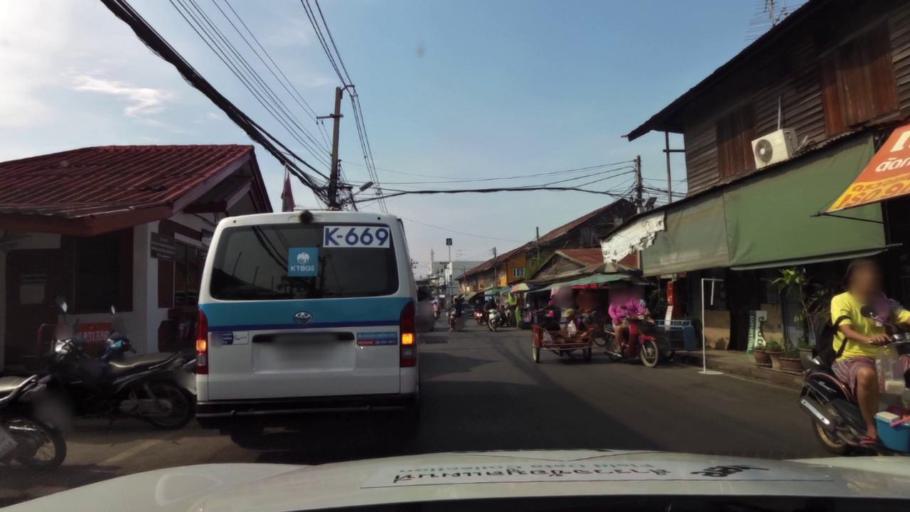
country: TH
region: Nakhon Sawan
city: Chumsaeng
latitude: 15.8908
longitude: 100.3072
